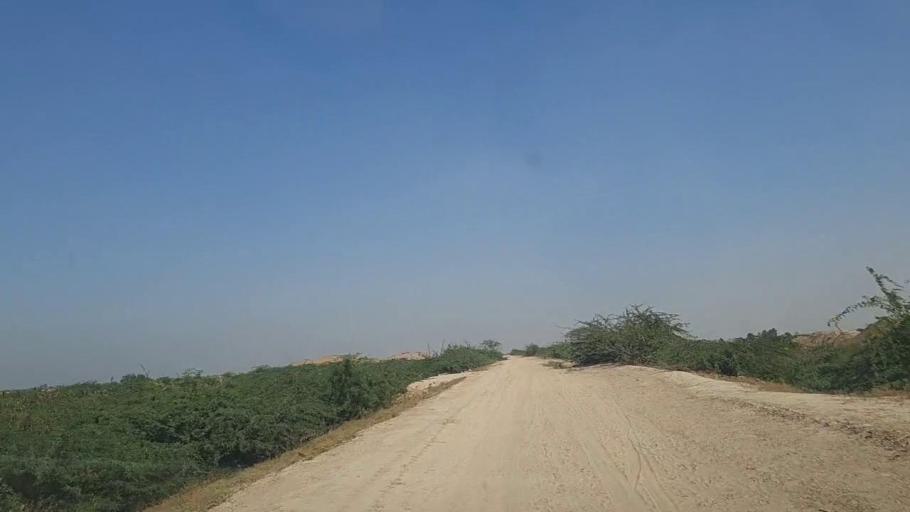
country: PK
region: Sindh
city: Daro Mehar
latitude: 24.8606
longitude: 68.0389
